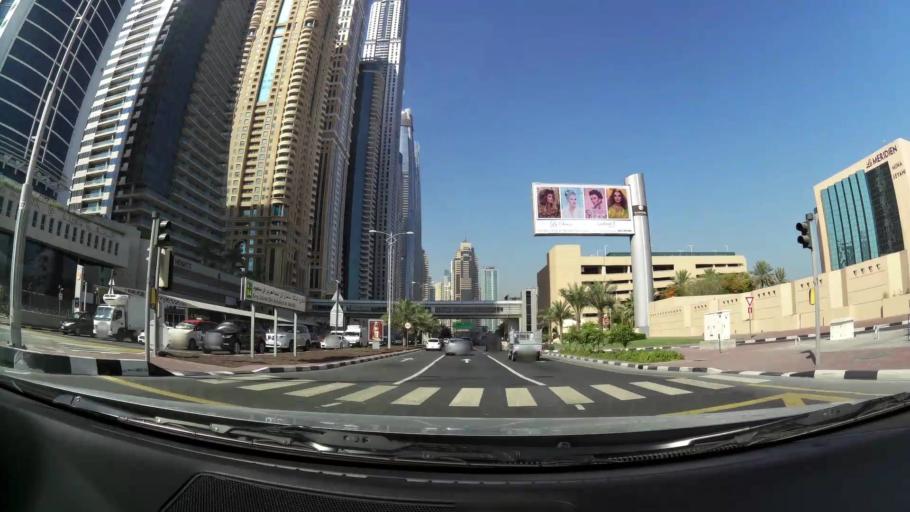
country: AE
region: Dubai
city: Dubai
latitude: 25.0918
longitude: 55.1488
